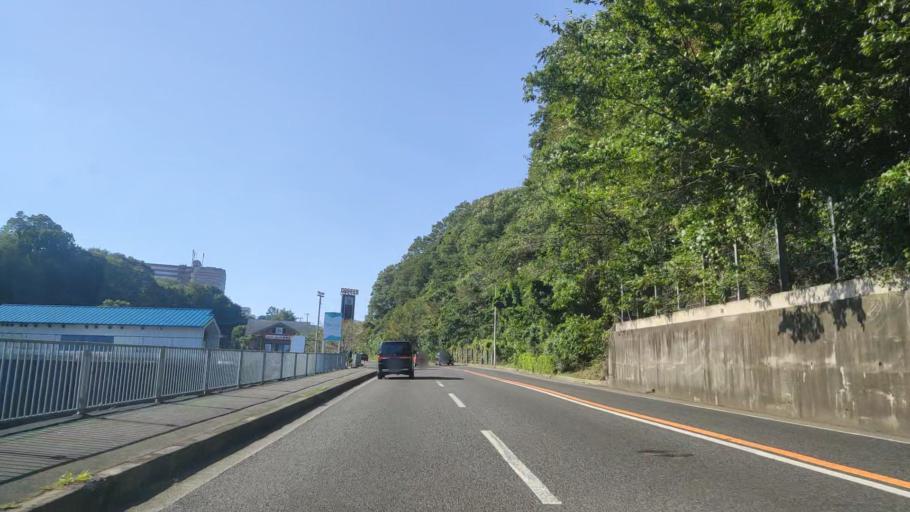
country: JP
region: Hyogo
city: Kobe
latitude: 34.7432
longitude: 135.1591
